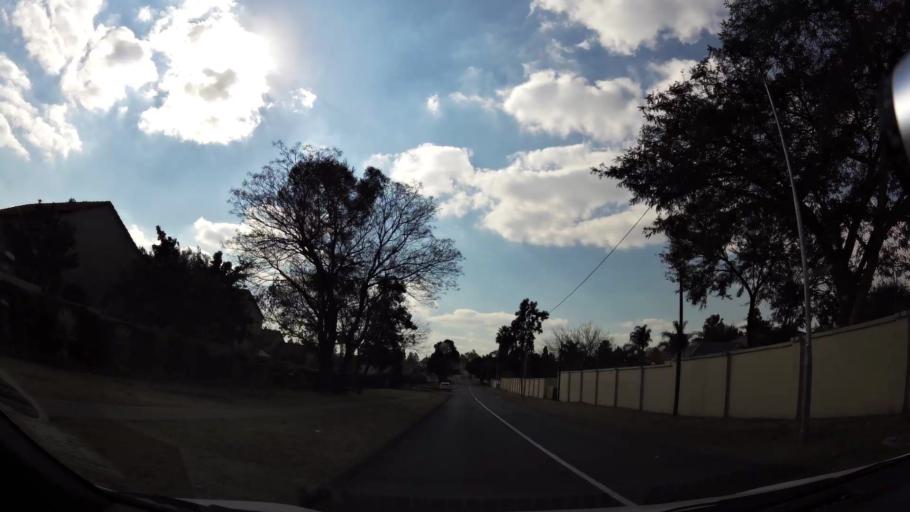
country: ZA
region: Gauteng
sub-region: City of Johannesburg Metropolitan Municipality
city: Midrand
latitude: -26.0217
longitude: 28.0712
